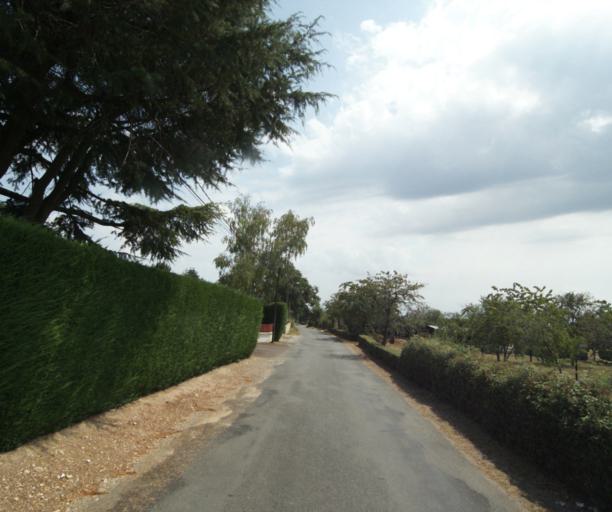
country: FR
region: Bourgogne
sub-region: Departement de Saone-et-Loire
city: Gueugnon
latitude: 46.6033
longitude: 4.0167
